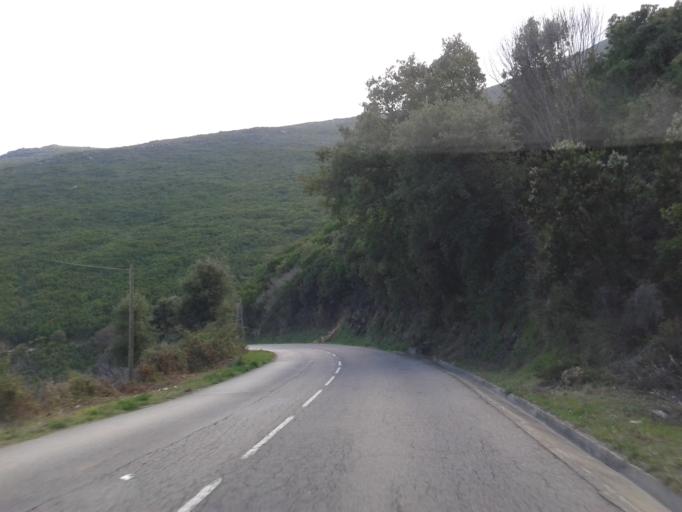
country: FR
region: Corsica
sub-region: Departement de la Haute-Corse
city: Biguglia
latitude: 42.5989
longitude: 9.4104
